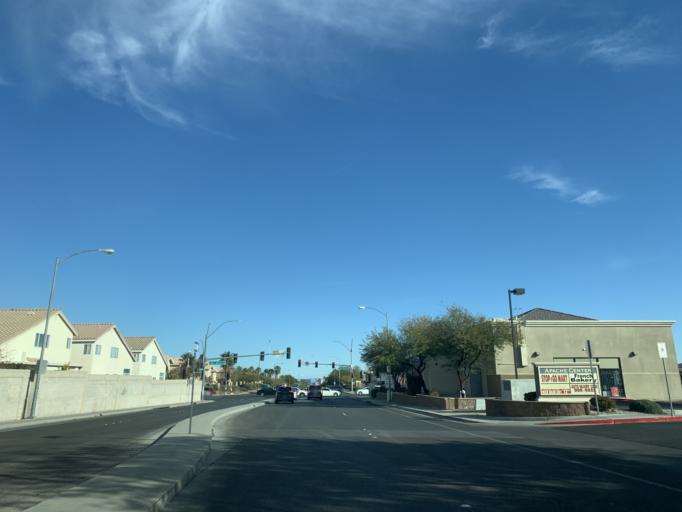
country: US
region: Nevada
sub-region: Clark County
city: Summerlin South
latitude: 36.1261
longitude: -115.2982
